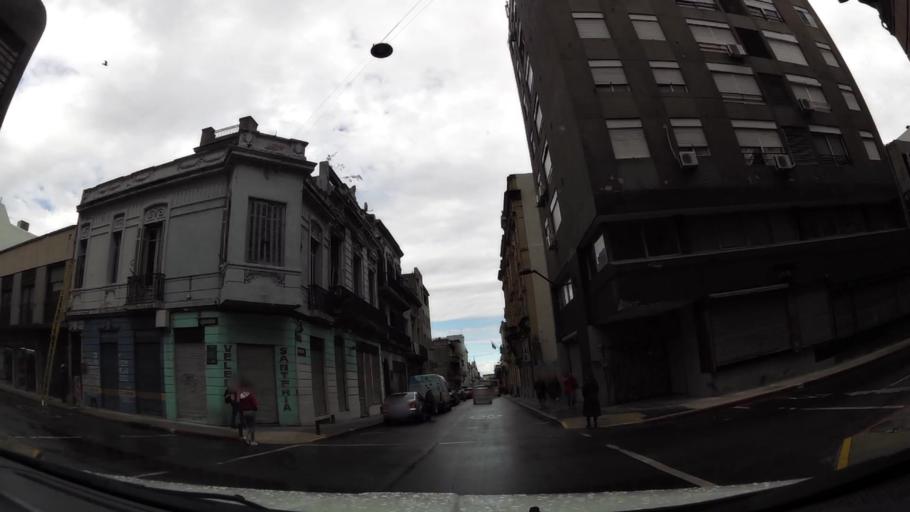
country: UY
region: Montevideo
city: Montevideo
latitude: -34.9072
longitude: -56.2096
